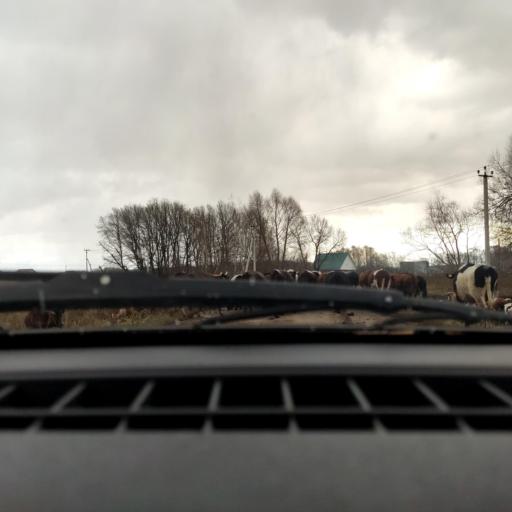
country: RU
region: Bashkortostan
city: Iglino
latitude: 54.7405
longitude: 56.3230
